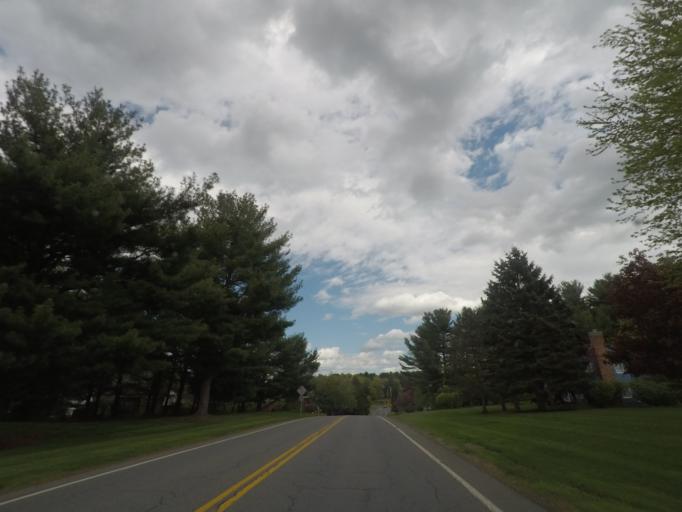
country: US
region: New York
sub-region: Albany County
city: Voorheesville
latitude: 42.6712
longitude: -73.9162
